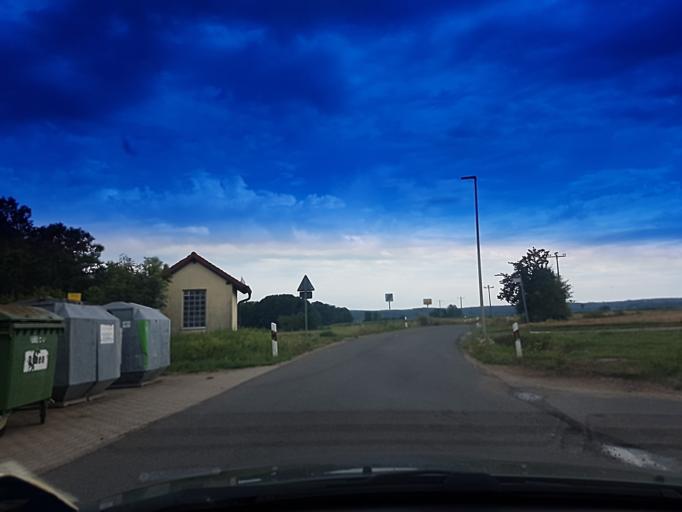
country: DE
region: Bavaria
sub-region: Upper Franconia
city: Frensdorf
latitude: 49.8335
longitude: 10.8620
